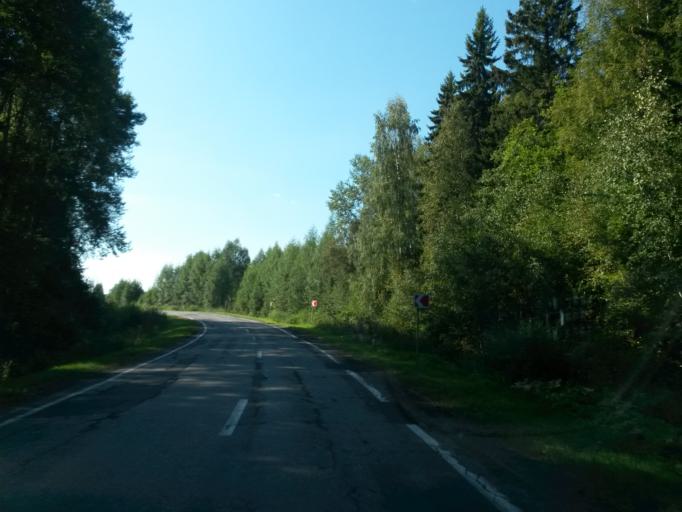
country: RU
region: Jaroslavl
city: Konstantinovskiy
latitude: 57.8050
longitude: 39.7795
